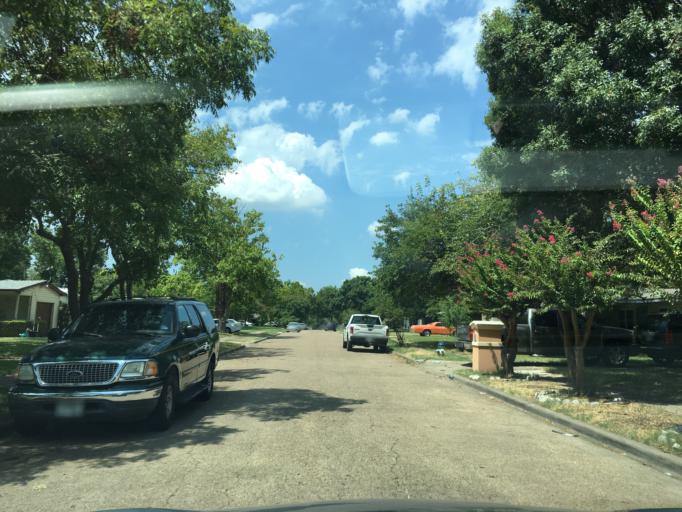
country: US
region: Texas
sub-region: Dallas County
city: Garland
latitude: 32.8625
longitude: -96.6756
